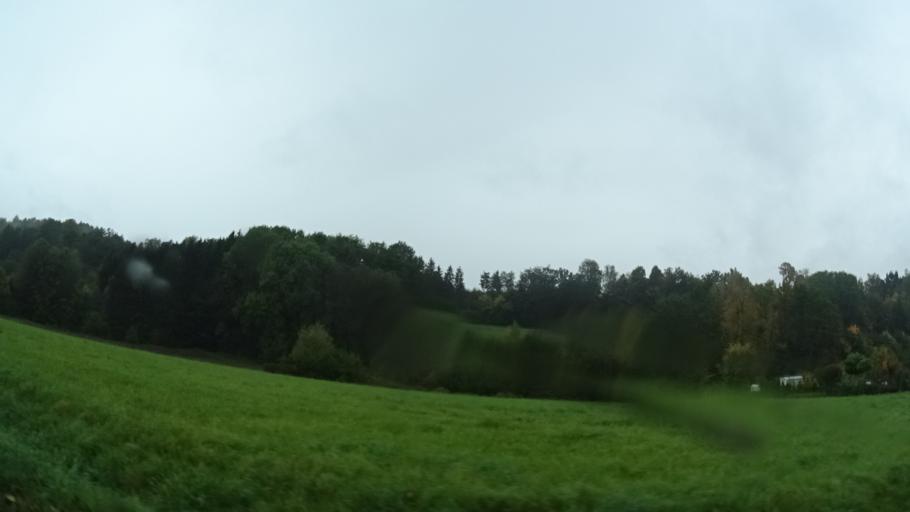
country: DE
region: Bavaria
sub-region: Upper Franconia
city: Kronach
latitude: 50.2502
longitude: 11.3379
